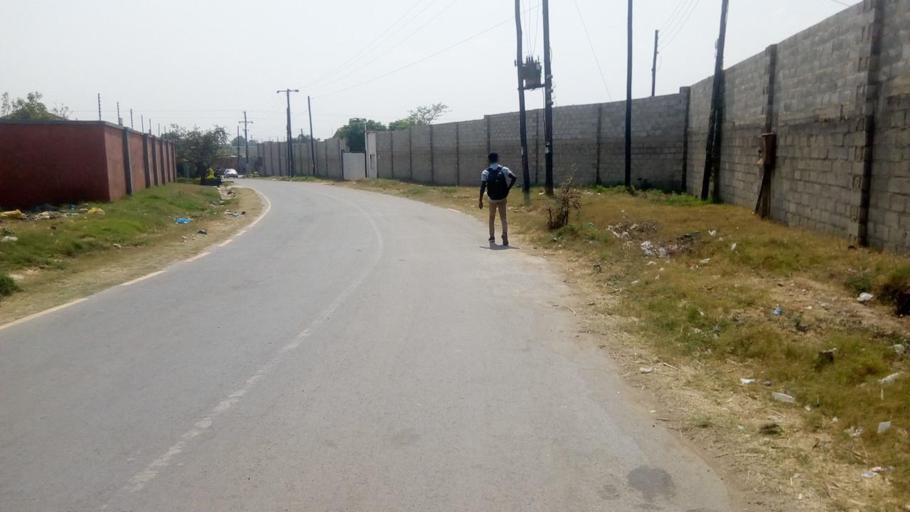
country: ZM
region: Lusaka
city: Lusaka
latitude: -15.3623
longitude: 28.2860
